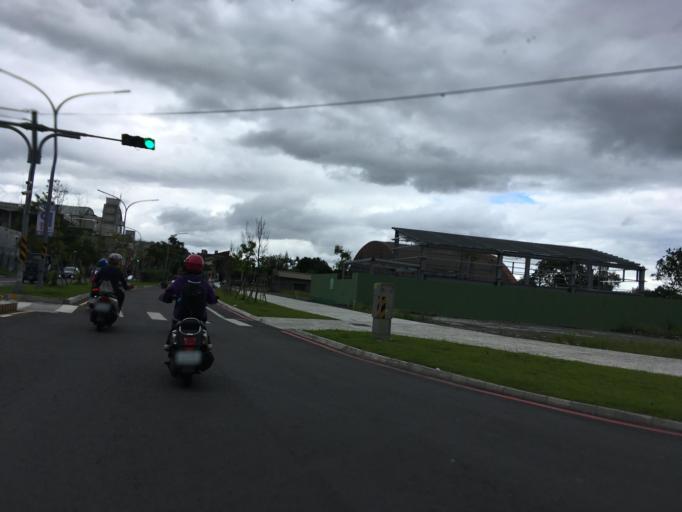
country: TW
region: Taiwan
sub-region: Yilan
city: Yilan
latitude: 24.6804
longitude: 121.7717
